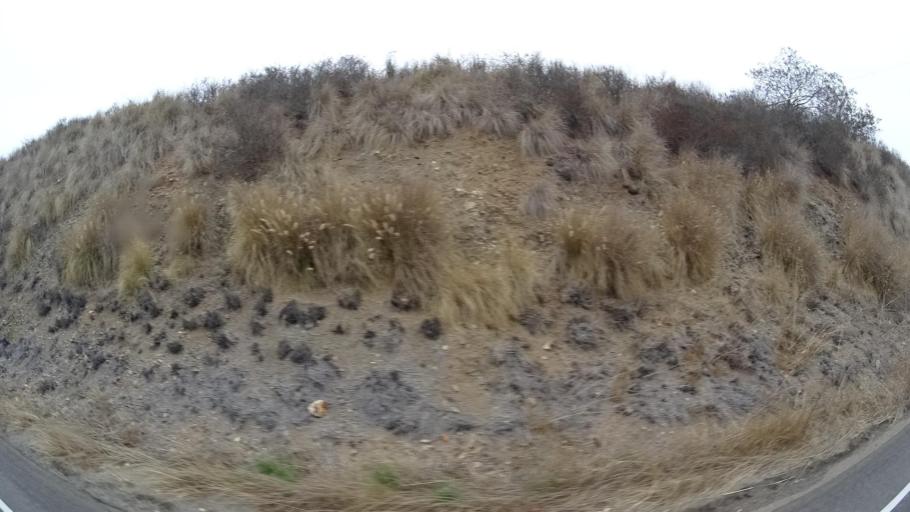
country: US
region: California
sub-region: San Diego County
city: Lake San Marcos
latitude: 33.0912
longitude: -117.1920
